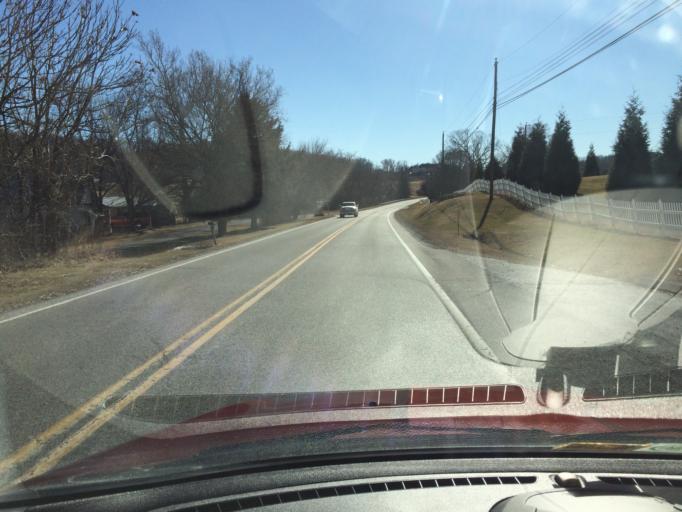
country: US
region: Virginia
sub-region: Augusta County
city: Weyers Cave
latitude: 38.3030
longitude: -78.9347
